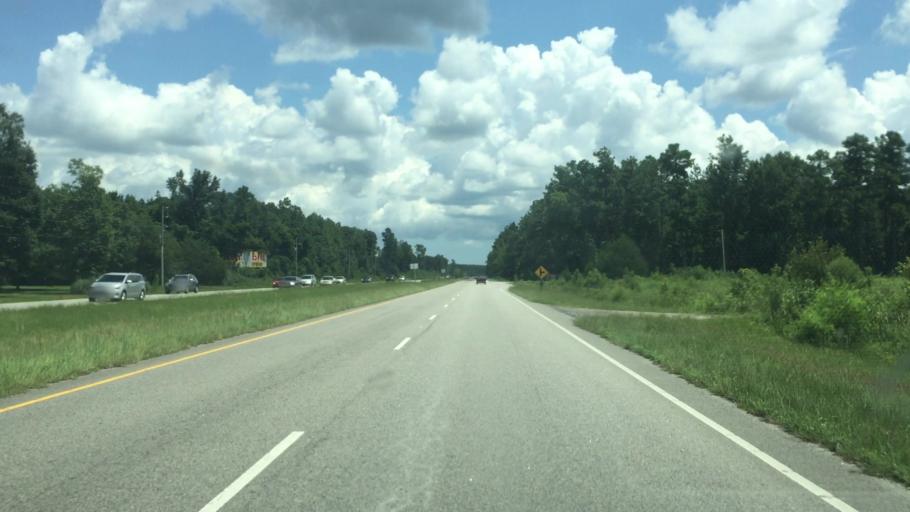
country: US
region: South Carolina
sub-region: Horry County
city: Loris
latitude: 34.0135
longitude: -78.7818
